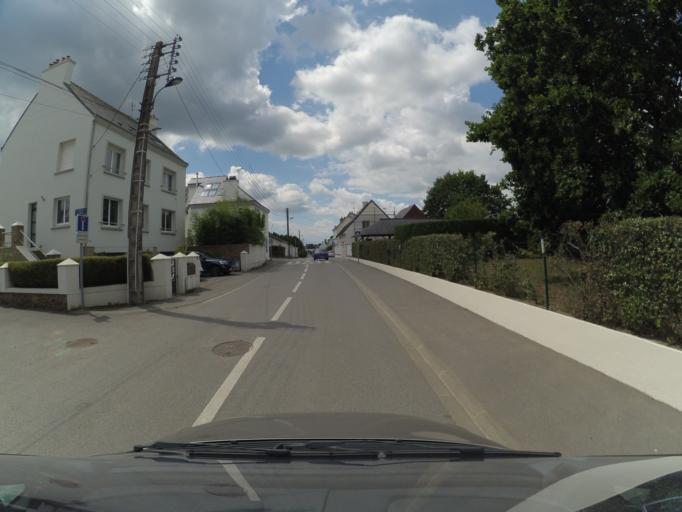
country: FR
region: Brittany
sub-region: Departement du Morbihan
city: Auray
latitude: 47.6796
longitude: -3.0030
